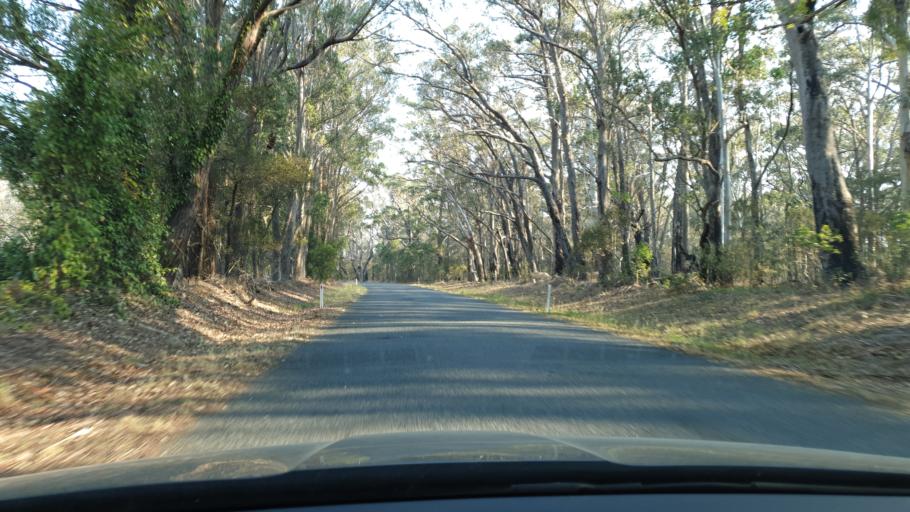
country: AU
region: New South Wales
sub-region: Tenterfield Municipality
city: Carrolls Creek
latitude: -28.6944
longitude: 152.0907
